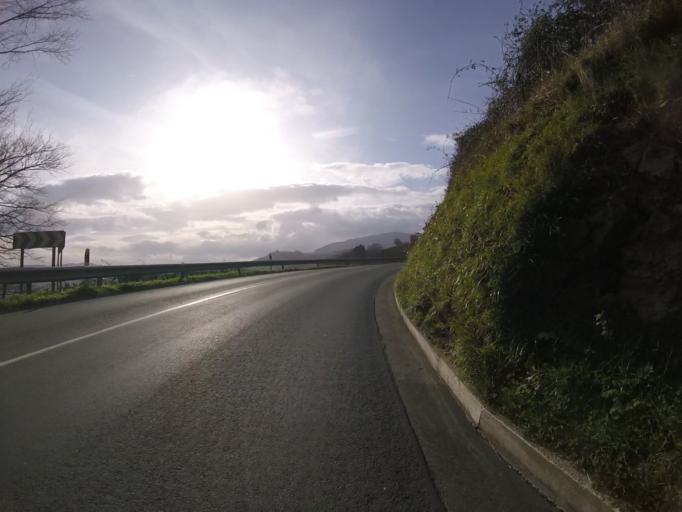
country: ES
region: Basque Country
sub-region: Provincia de Guipuzcoa
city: Asteasu
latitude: 43.2007
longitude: -2.1154
